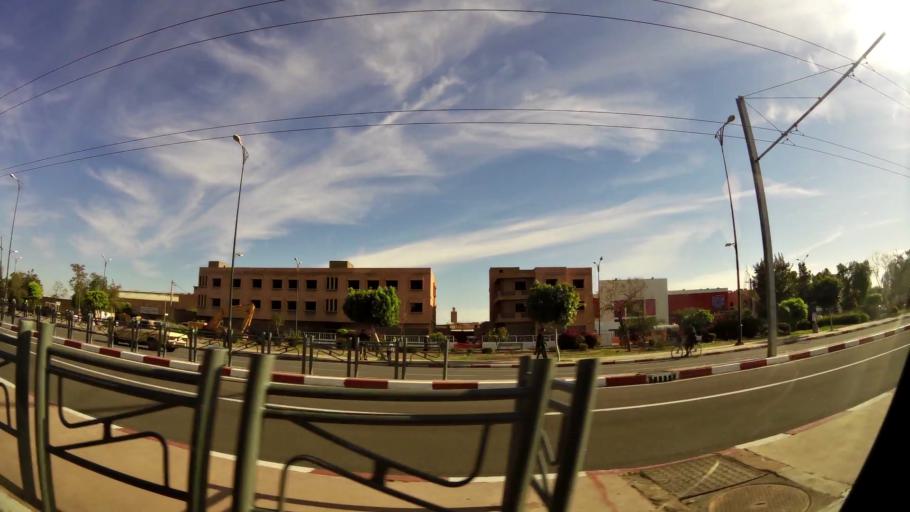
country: MA
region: Marrakech-Tensift-Al Haouz
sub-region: Marrakech
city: Marrakesh
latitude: 31.6277
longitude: -8.0470
